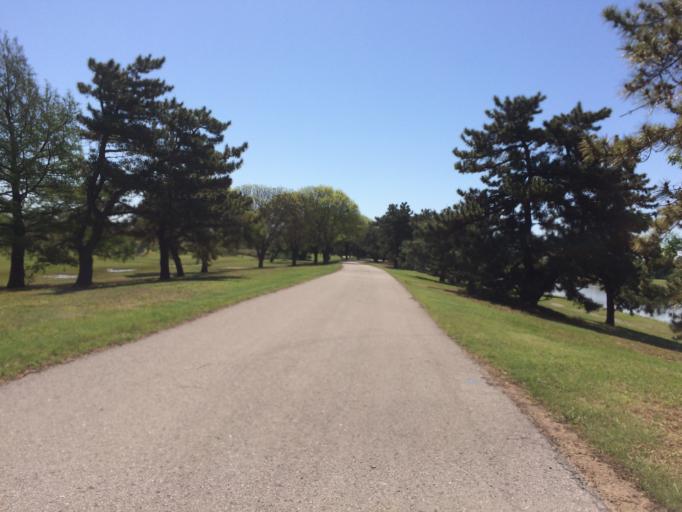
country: US
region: Oklahoma
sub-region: Oklahoma County
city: Oklahoma City
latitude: 35.4525
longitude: -97.5284
